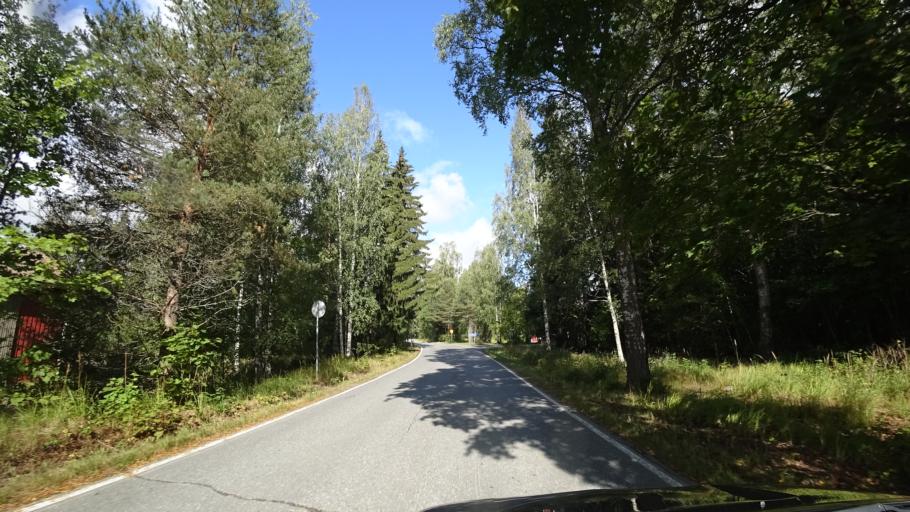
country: FI
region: Haeme
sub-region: Riihimaeki
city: Oitti
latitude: 60.6878
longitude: 25.0006
